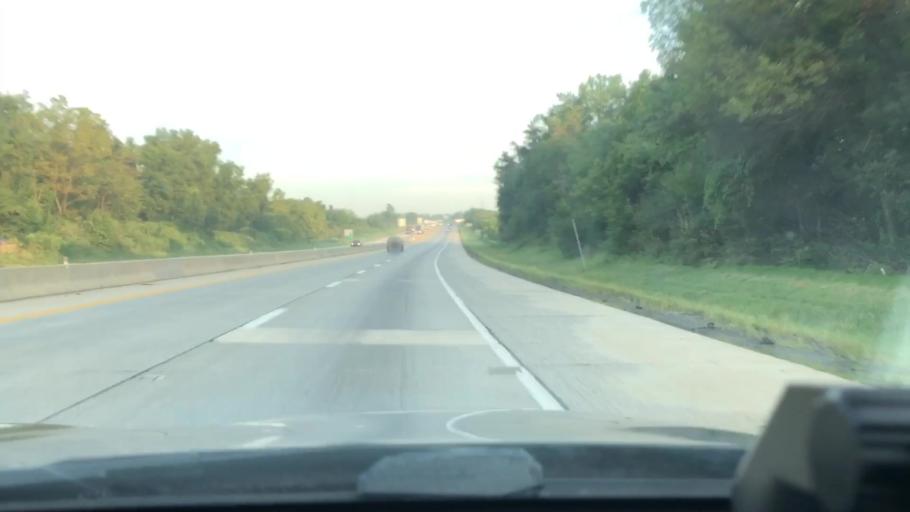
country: US
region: Pennsylvania
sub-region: Lehigh County
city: Wescosville
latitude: 40.5803
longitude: -75.5643
